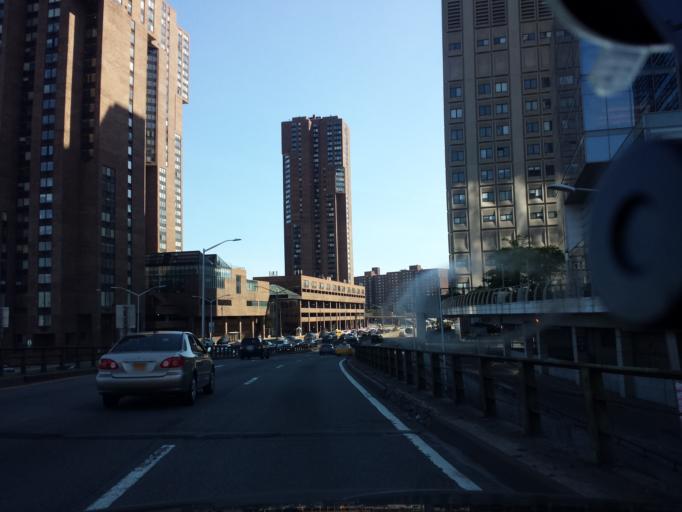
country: US
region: New York
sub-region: Queens County
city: Long Island City
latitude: 40.7397
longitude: -73.9732
